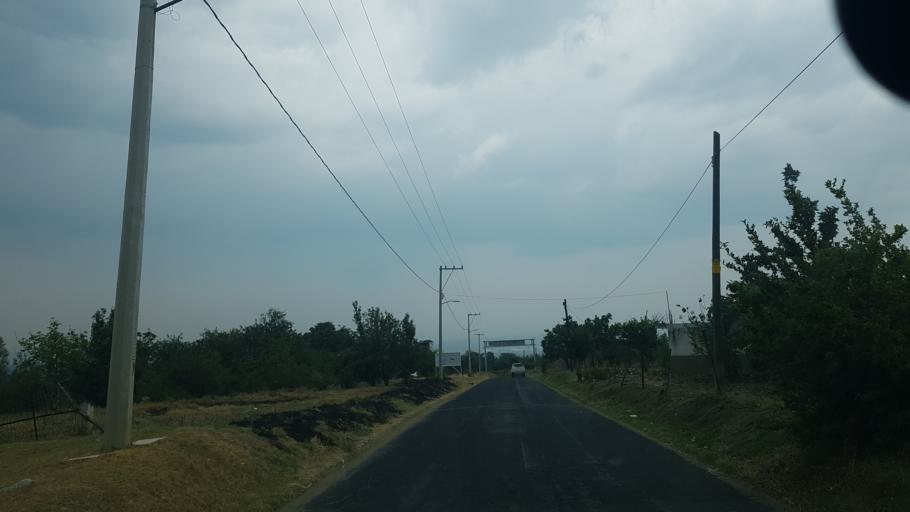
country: MX
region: Puebla
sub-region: Chiautzingo
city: San Nicolas Zecalacoayan
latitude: 19.1800
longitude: -98.4847
